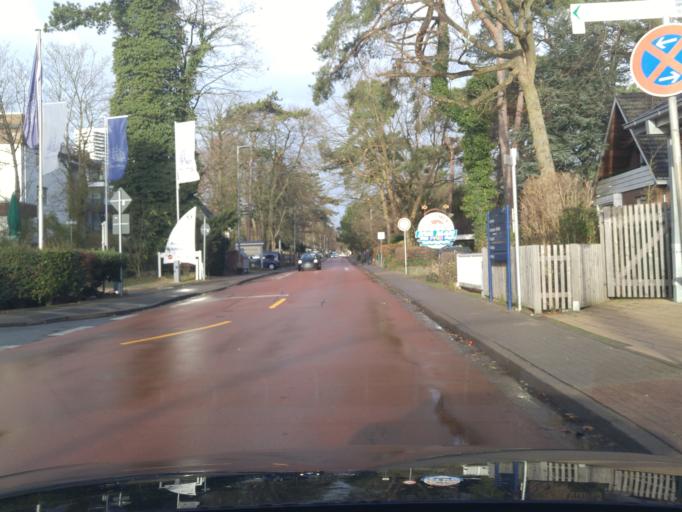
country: DE
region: Schleswig-Holstein
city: Timmendorfer Strand
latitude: 54.0021
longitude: 10.7778
